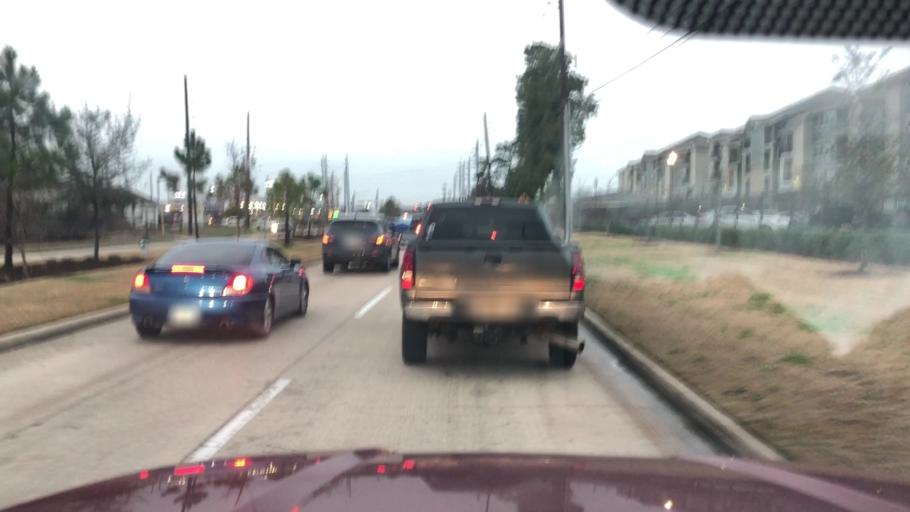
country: US
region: Texas
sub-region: Harris County
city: Tomball
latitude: 30.0436
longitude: -95.5381
